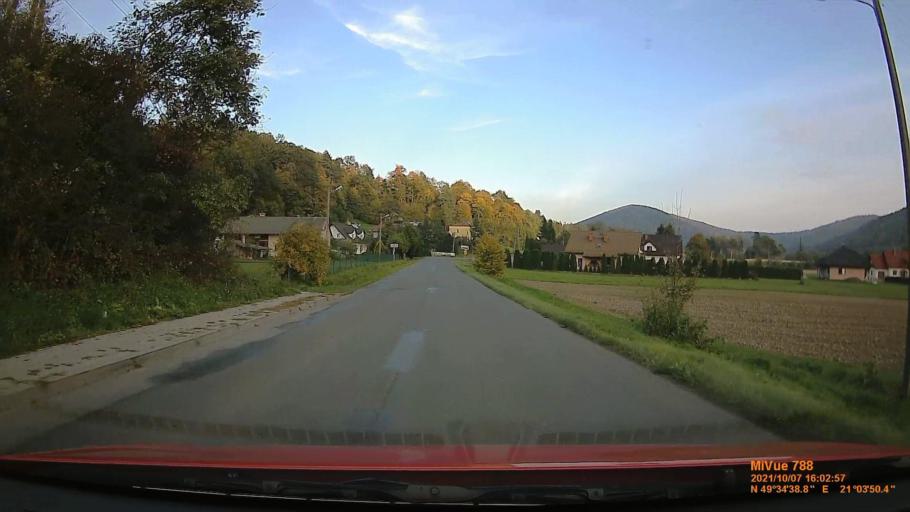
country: PL
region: Lesser Poland Voivodeship
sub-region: Powiat gorlicki
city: Ropa
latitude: 49.5774
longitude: 21.0640
